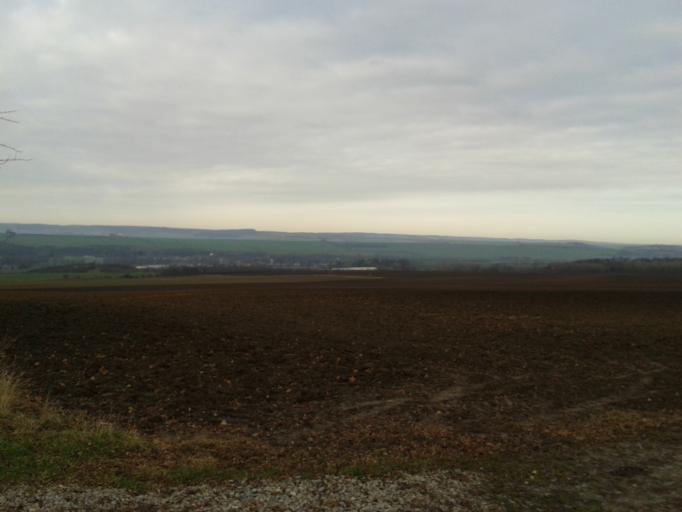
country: DE
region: Thuringia
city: Eberstedt
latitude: 51.0499
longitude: 11.5846
